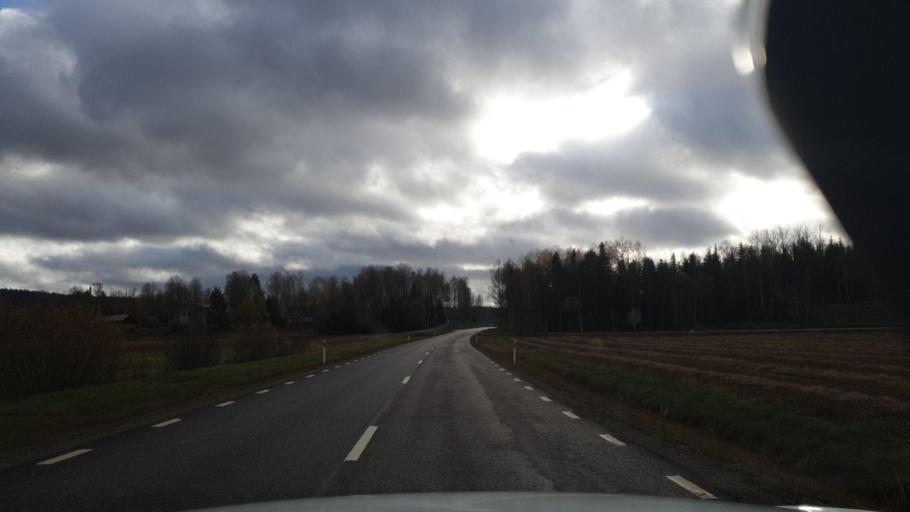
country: SE
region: Vaermland
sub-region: Arvika Kommun
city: Arvika
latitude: 59.4782
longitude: 12.7692
